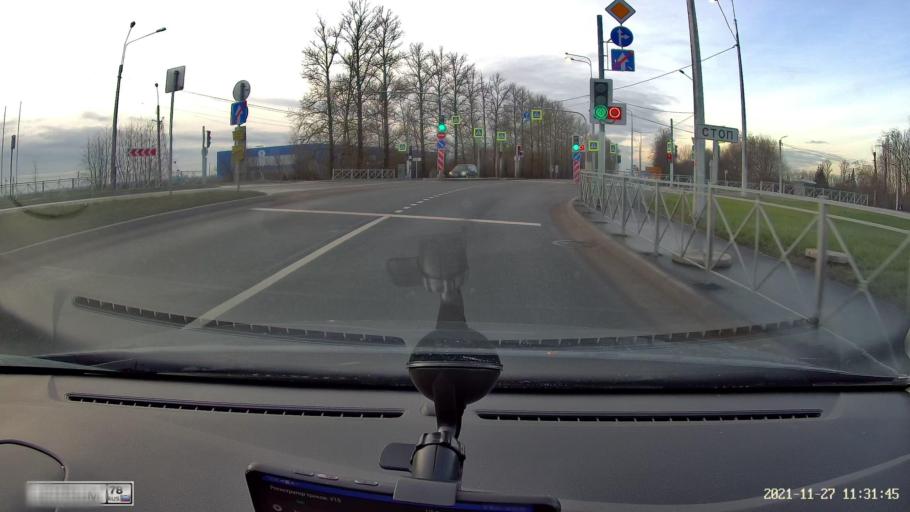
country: RU
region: St.-Petersburg
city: Krasnoye Selo
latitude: 59.7169
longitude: 30.0466
